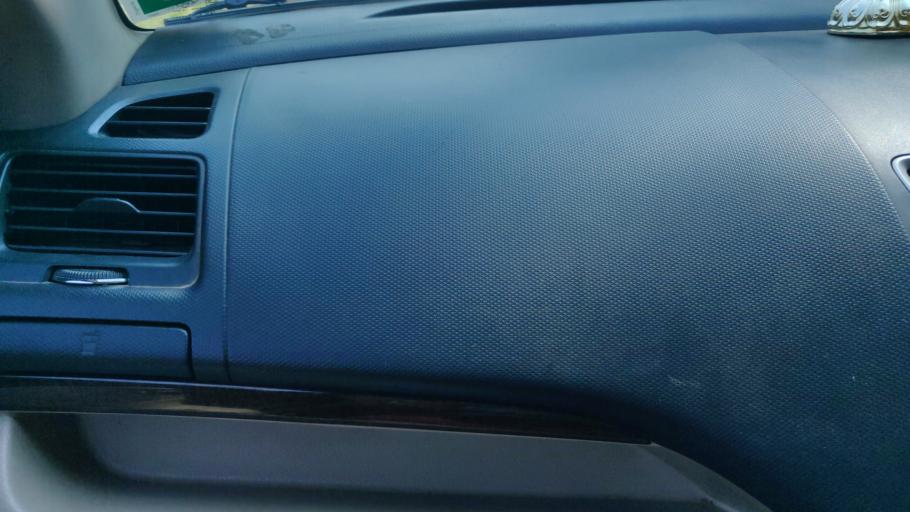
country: IN
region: Karnataka
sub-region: Dakshina Kannada
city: Ullal
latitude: 12.8529
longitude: 74.8369
